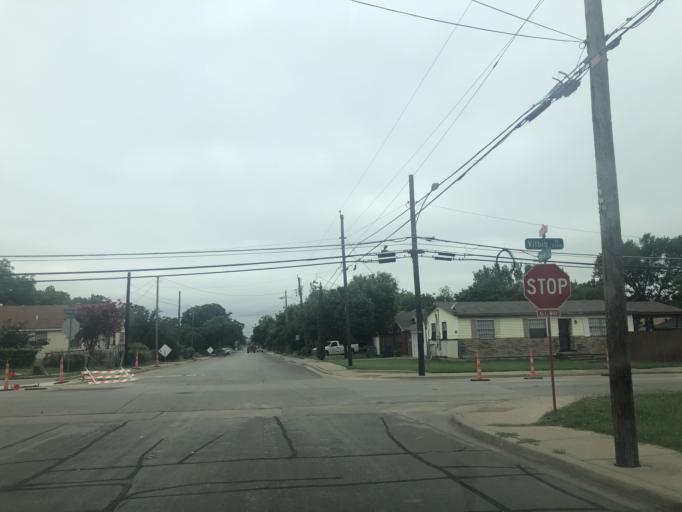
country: US
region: Texas
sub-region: Dallas County
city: Dallas
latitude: 32.7818
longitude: -96.8479
